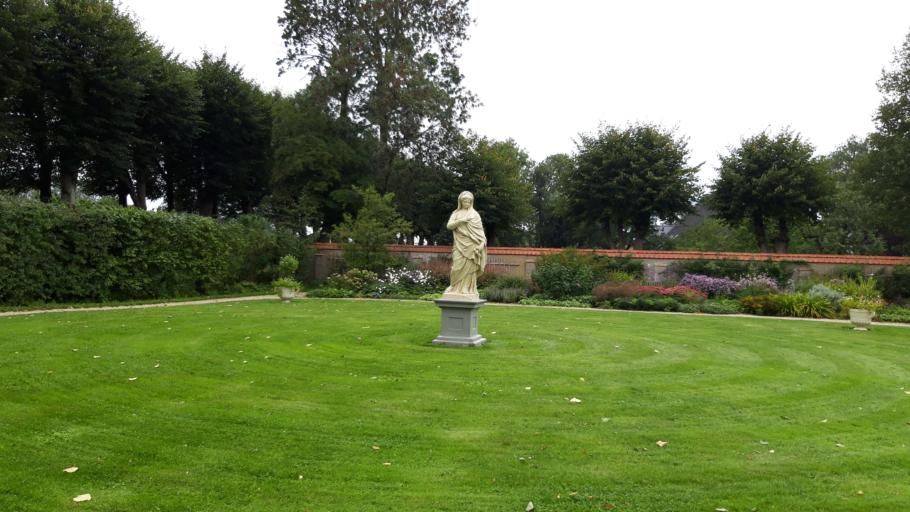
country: NL
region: Friesland
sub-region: Gemeente Leeuwarderadeel
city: Britsum
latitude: 53.2331
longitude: 5.7832
